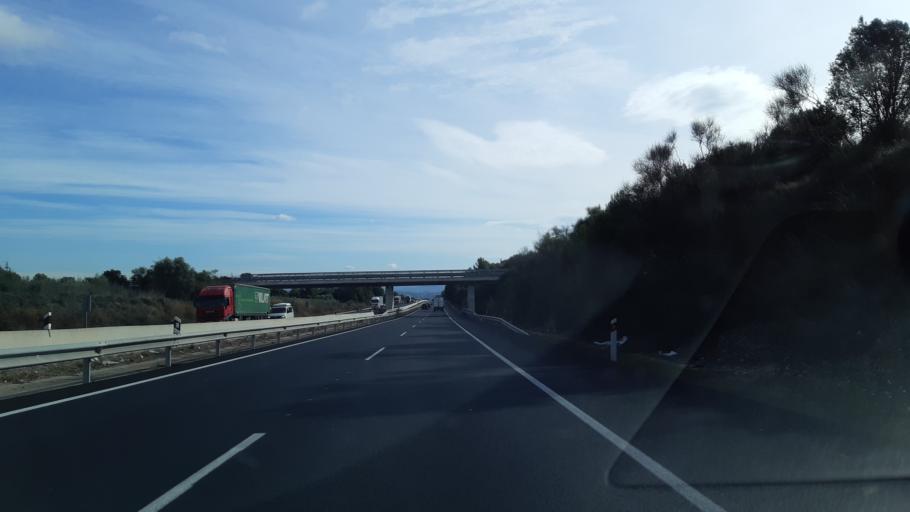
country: ES
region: Catalonia
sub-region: Provincia de Barcelona
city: Collbato
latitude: 41.5532
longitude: 1.8411
